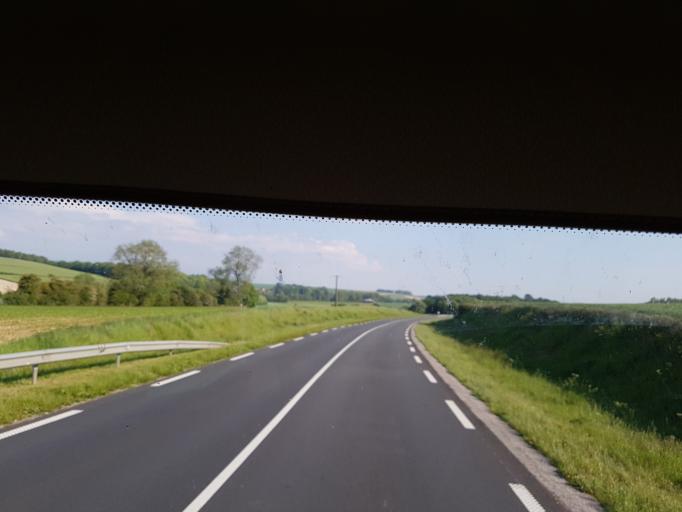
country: FR
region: Picardie
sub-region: Departement de la Somme
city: Crecy-en-Ponthieu
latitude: 50.1829
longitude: 1.8713
